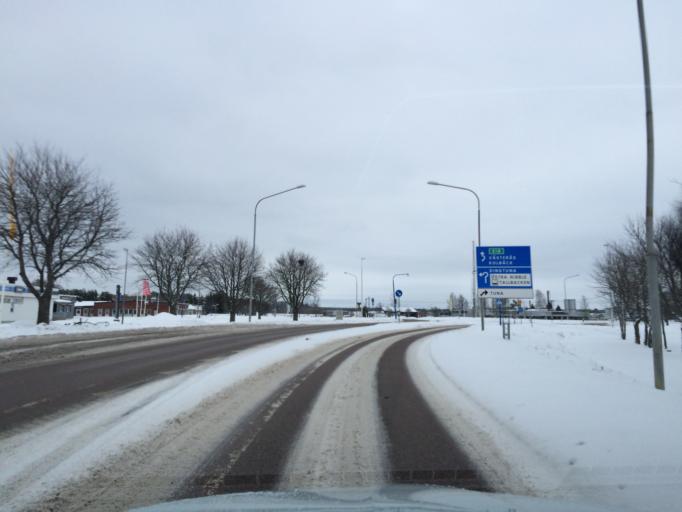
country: SE
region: Vaestmanland
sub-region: Hallstahammars Kommun
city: Hallstahammar
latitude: 59.6095
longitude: 16.2436
